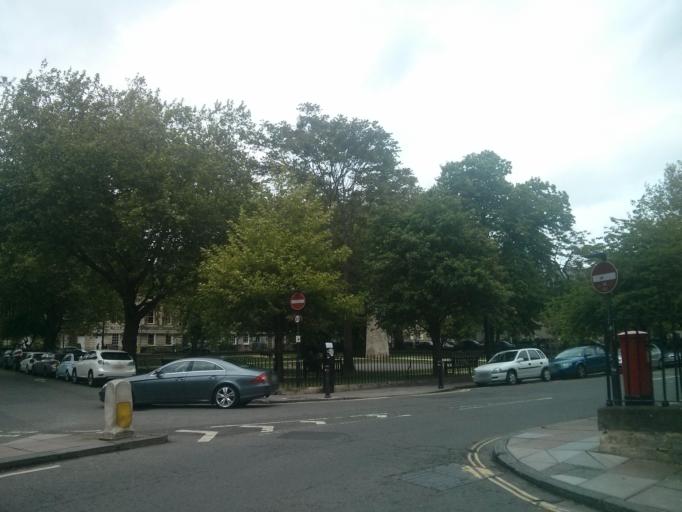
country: GB
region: England
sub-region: Bath and North East Somerset
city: Bath
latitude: 51.3830
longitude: -2.3642
